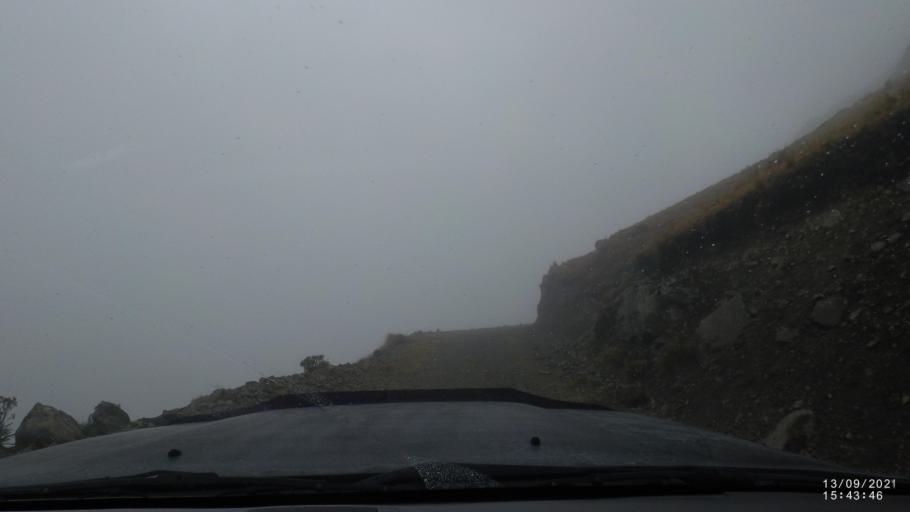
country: BO
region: Cochabamba
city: Colomi
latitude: -17.3216
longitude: -65.7199
